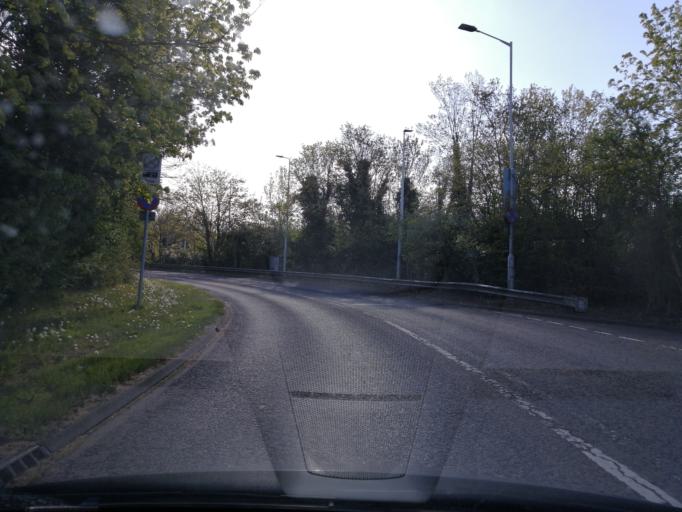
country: GB
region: England
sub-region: Peterborough
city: Peterborough
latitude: 52.6018
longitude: -0.2509
